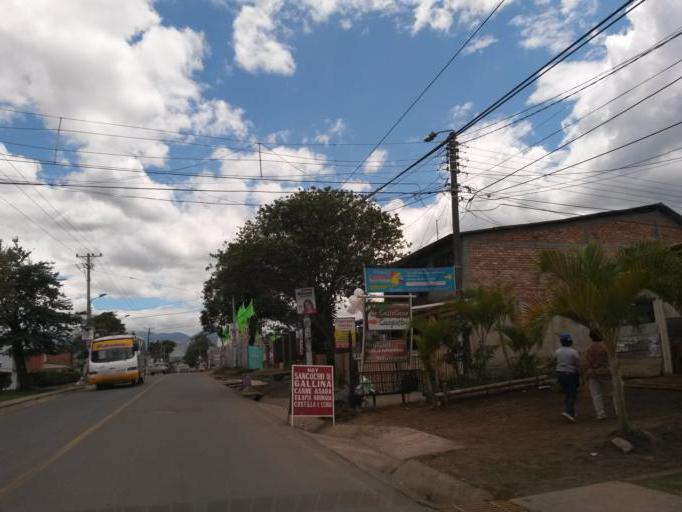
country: CO
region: Cauca
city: Popayan
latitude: 2.4858
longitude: -76.5832
